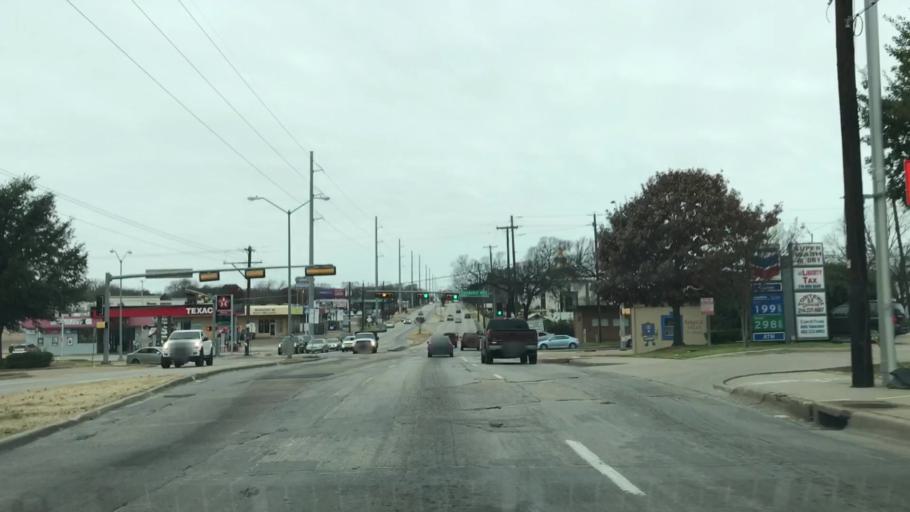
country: US
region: Texas
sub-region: Dallas County
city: Cockrell Hill
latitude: 32.7205
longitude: -96.8908
